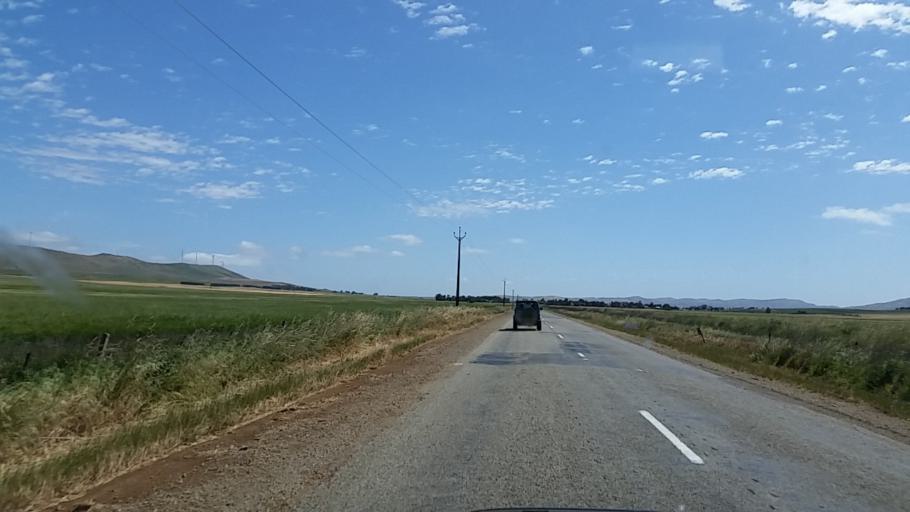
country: AU
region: South Australia
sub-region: Clare and Gilbert Valleys
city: Clare
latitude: -33.5688
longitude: 138.8895
